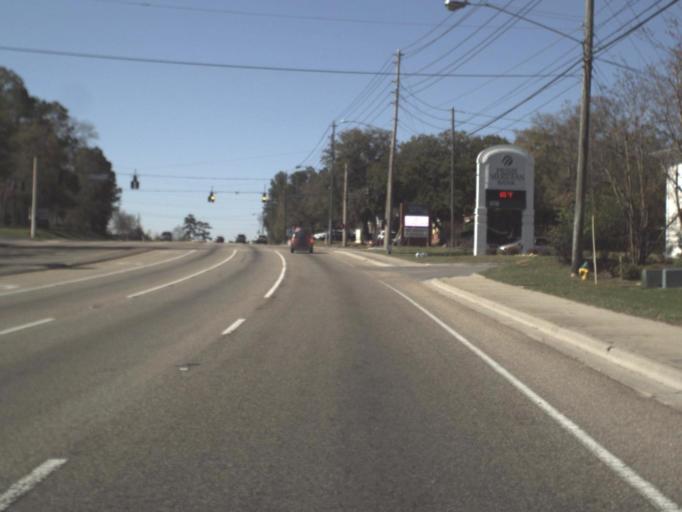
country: US
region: Florida
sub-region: Leon County
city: Tallahassee
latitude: 30.4718
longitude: -84.2318
